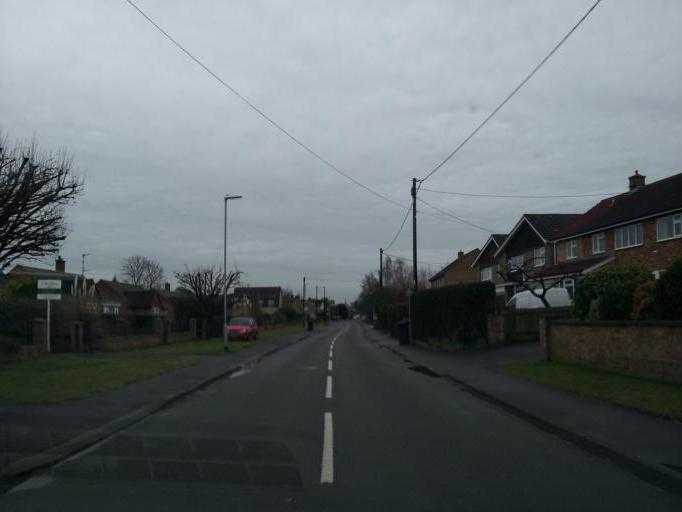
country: GB
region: England
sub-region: Cambridgeshire
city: Bottisham
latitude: 52.2272
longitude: 0.2535
